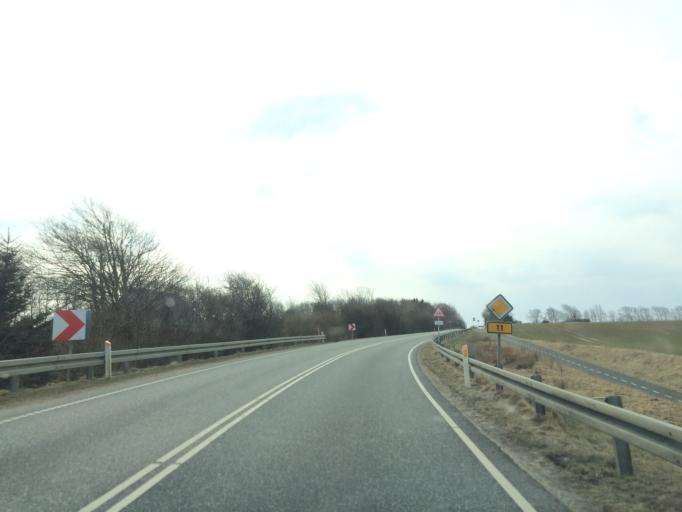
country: DK
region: Central Jutland
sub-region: Ringkobing-Skjern Kommune
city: Videbaek
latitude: 56.1070
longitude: 8.5076
